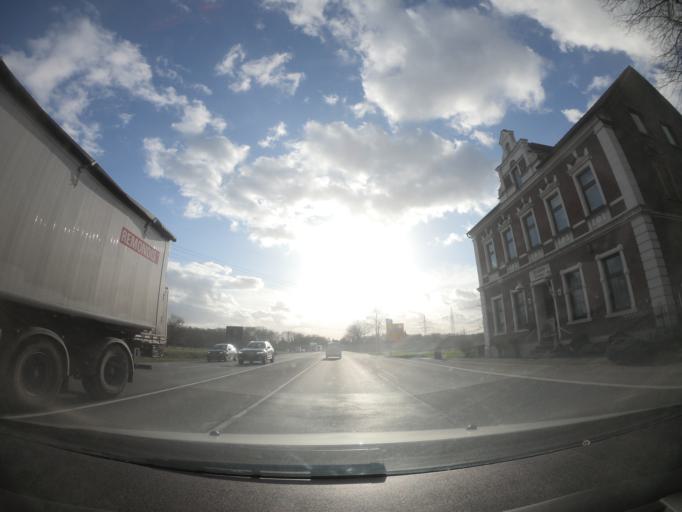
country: DE
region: North Rhine-Westphalia
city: Lunen
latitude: 51.5933
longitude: 7.4796
